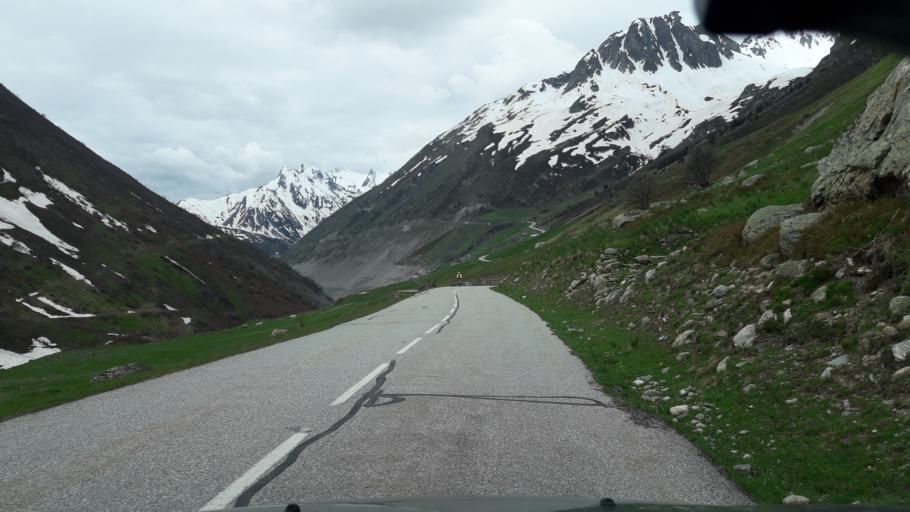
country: FR
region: Rhone-Alpes
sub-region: Departement de la Savoie
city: Saint-Etienne-de-Cuines
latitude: 45.2300
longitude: 6.1590
